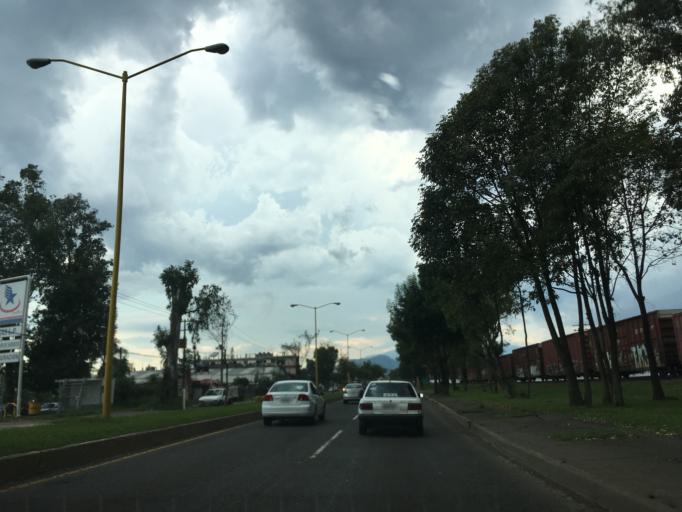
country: MX
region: Michoacan
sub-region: Uruapan
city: Toreo Bajo (El Toreo Bajo)
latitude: 19.4239
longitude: -102.0199
